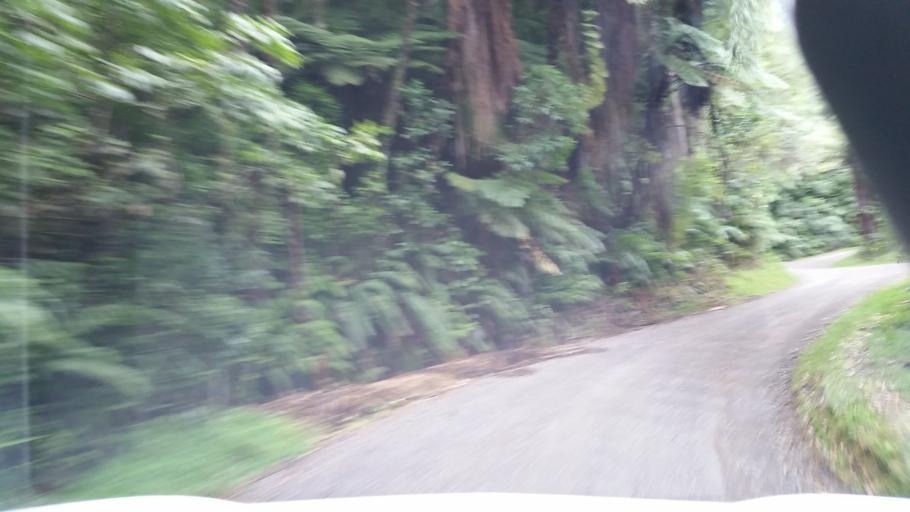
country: NZ
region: Bay of Plenty
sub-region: Rotorua District
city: Rotorua
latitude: -38.1581
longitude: 176.3644
